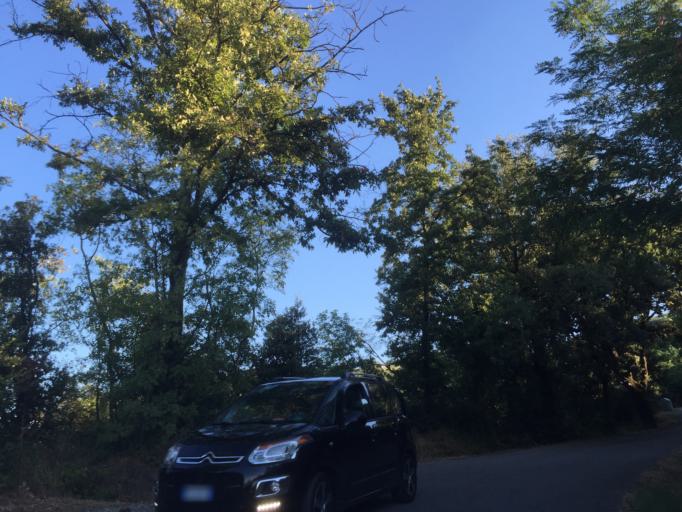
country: IT
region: Tuscany
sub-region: Provincia di Pistoia
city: Pistoia
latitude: 43.9478
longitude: 10.9583
